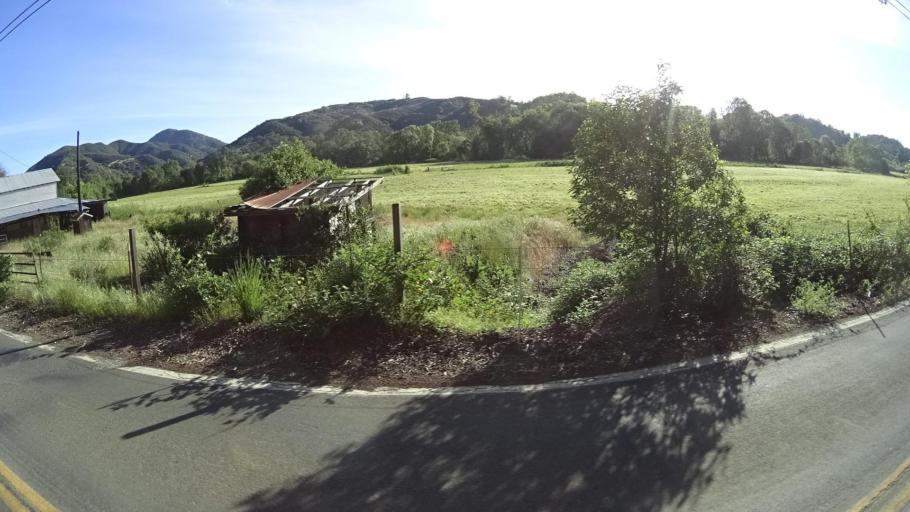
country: US
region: California
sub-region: Lake County
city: North Lakeport
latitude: 39.1168
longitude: -122.9881
